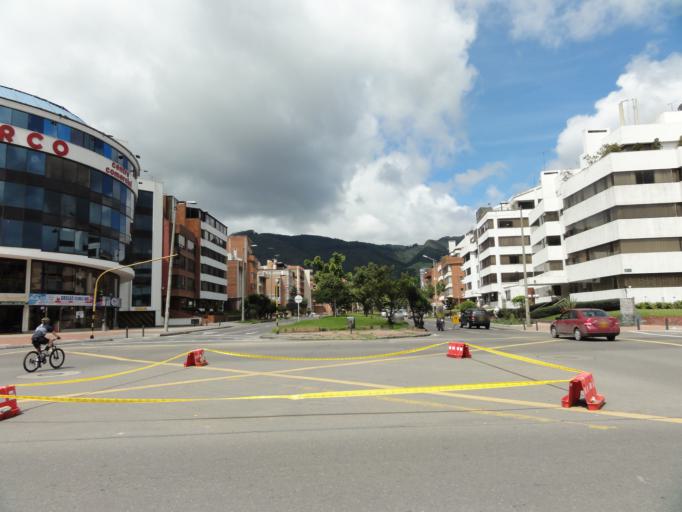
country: CO
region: Bogota D.C.
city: Barrio San Luis
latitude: 4.6962
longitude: -74.0434
